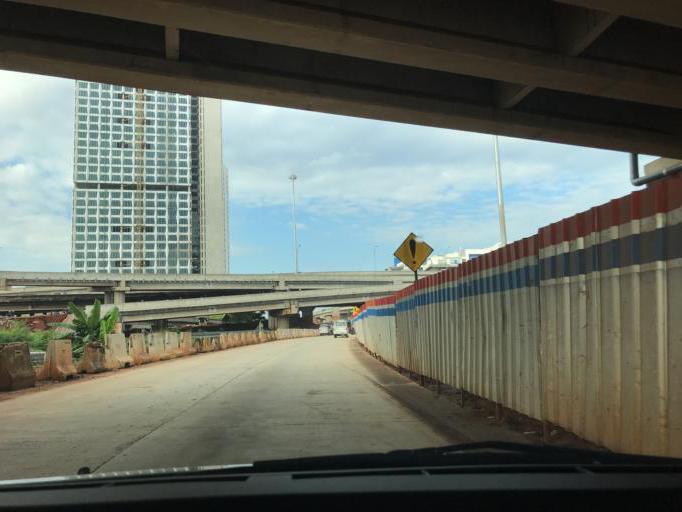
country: ID
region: West Java
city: Pamulang
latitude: -6.2911
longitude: 106.8058
